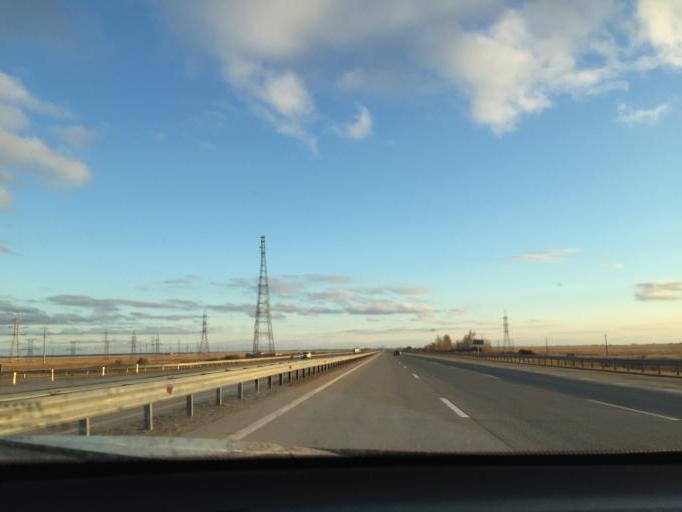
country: KZ
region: Astana Qalasy
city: Astana
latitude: 51.3007
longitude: 71.3555
